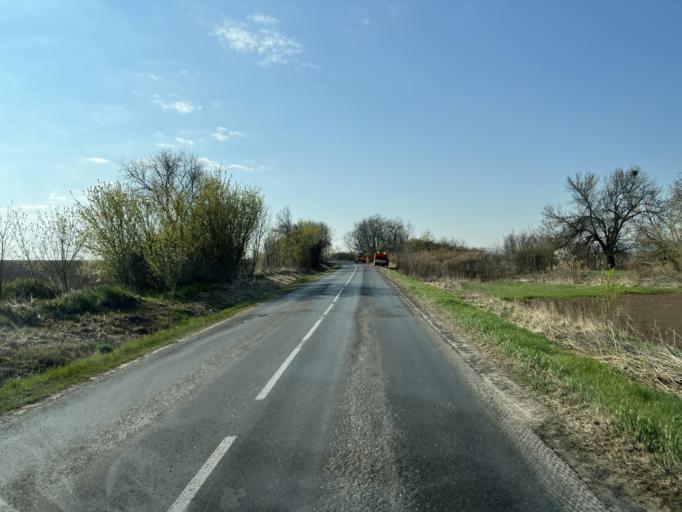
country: HU
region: Pest
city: Galgamacsa
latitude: 47.7169
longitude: 19.3821
